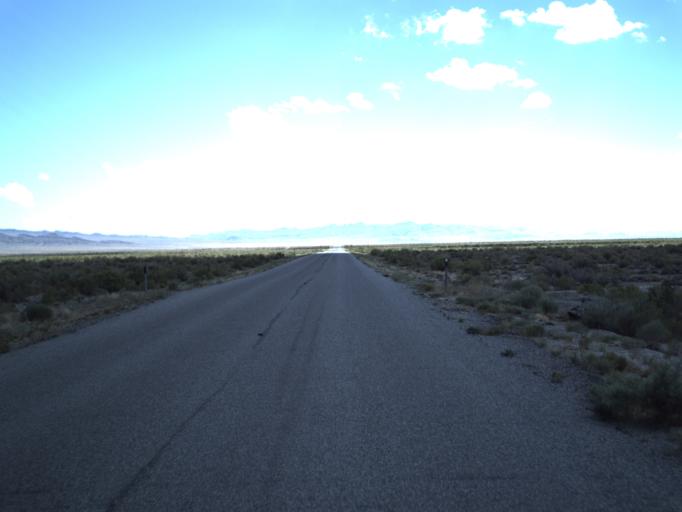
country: US
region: Nevada
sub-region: White Pine County
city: McGill
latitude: 39.0519
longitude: -113.9802
